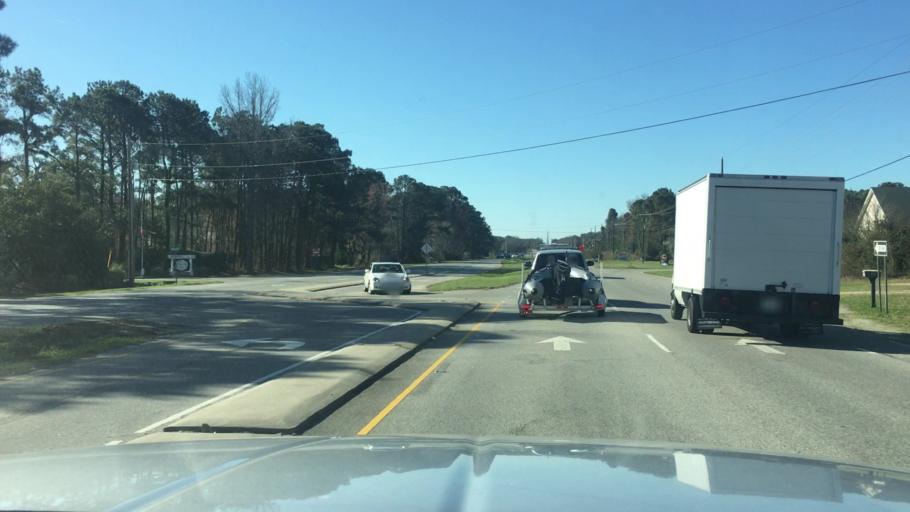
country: US
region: North Carolina
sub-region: New Hanover County
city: Sea Breeze
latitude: 34.0697
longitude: -77.8968
